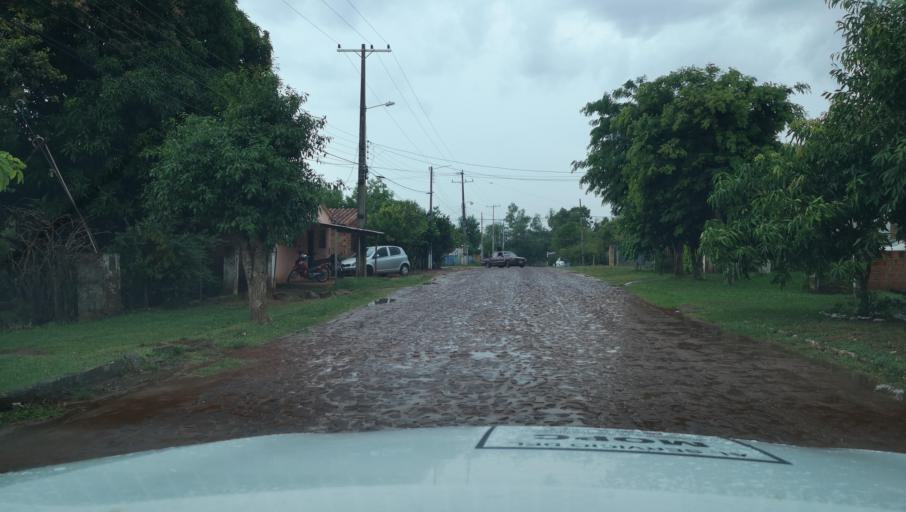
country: PY
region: Misiones
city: Santa Maria
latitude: -26.8960
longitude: -57.0328
